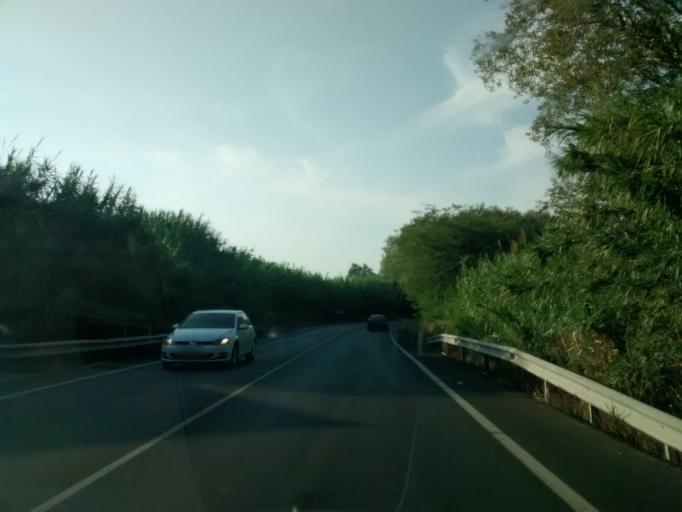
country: ES
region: Andalusia
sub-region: Provincia de Cadiz
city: Vejer de la Frontera
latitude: 36.2569
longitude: -5.9599
